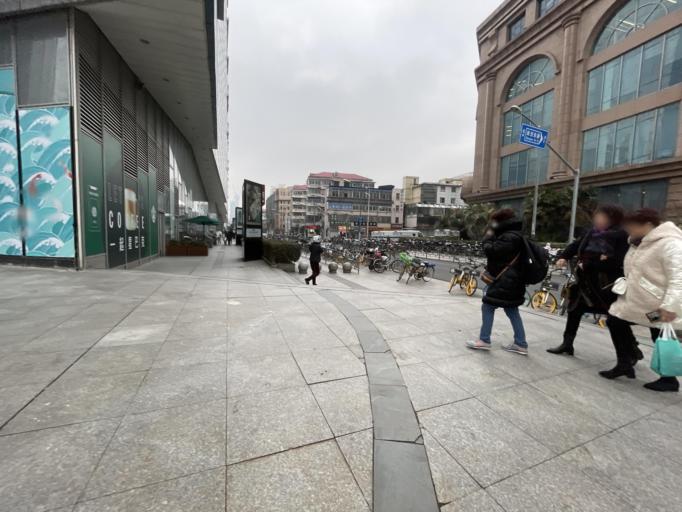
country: CN
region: Shanghai Shi
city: Yangpu
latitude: 31.3028
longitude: 121.5121
